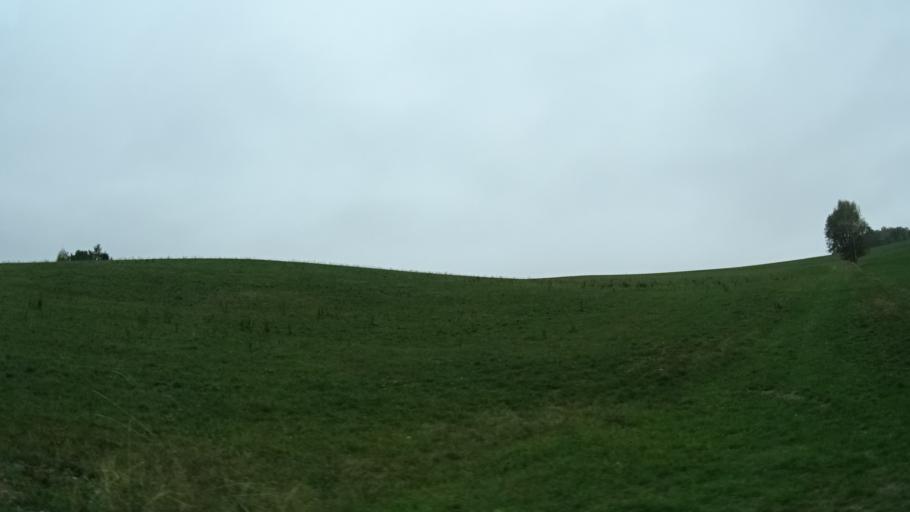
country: DE
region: Hesse
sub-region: Regierungsbezirk Kassel
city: Poppenhausen
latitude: 50.5051
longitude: 9.8685
